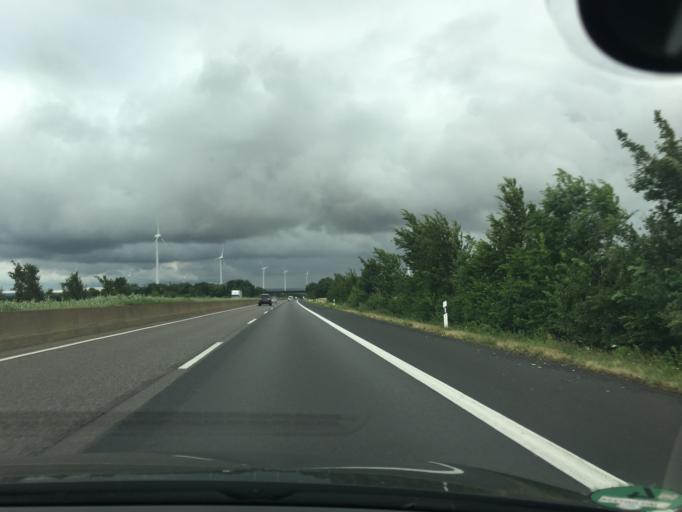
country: DE
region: North Rhine-Westphalia
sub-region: Regierungsbezirk Koln
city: Euskirchen
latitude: 50.7056
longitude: 6.7729
